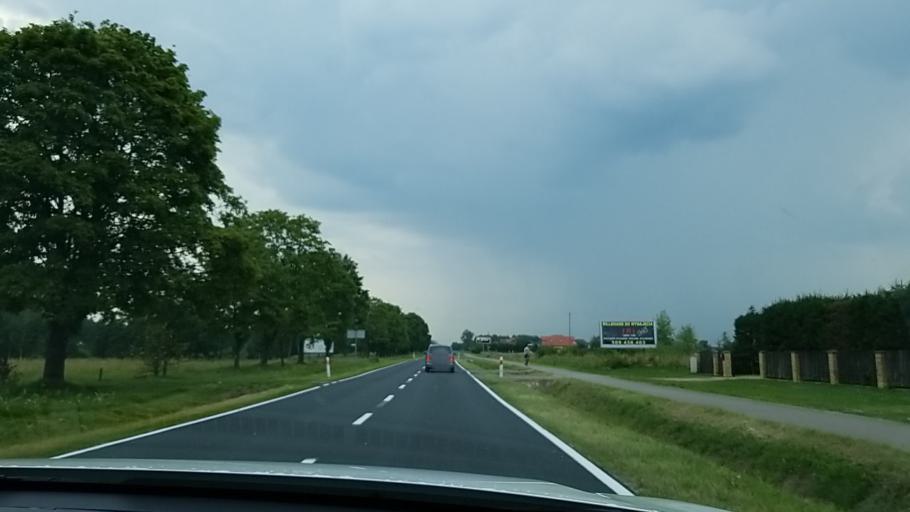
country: PL
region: Lublin Voivodeship
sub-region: Powiat wlodawski
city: Wlodawa
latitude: 51.5680
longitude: 23.5485
